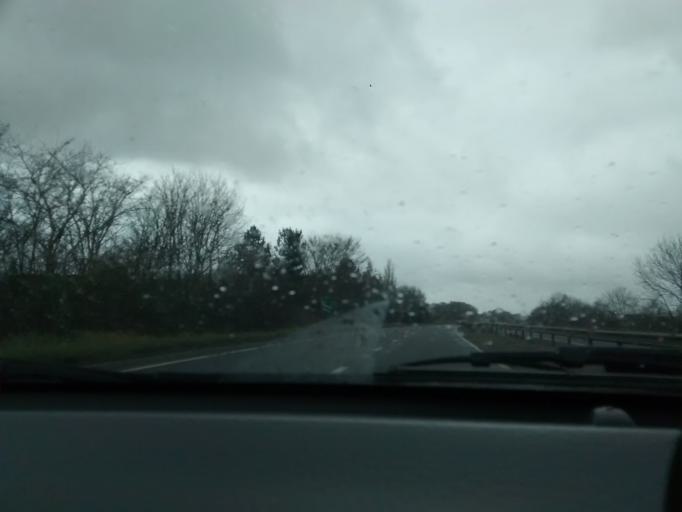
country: GB
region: England
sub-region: Suffolk
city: Felixstowe
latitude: 51.9828
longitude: 1.3246
